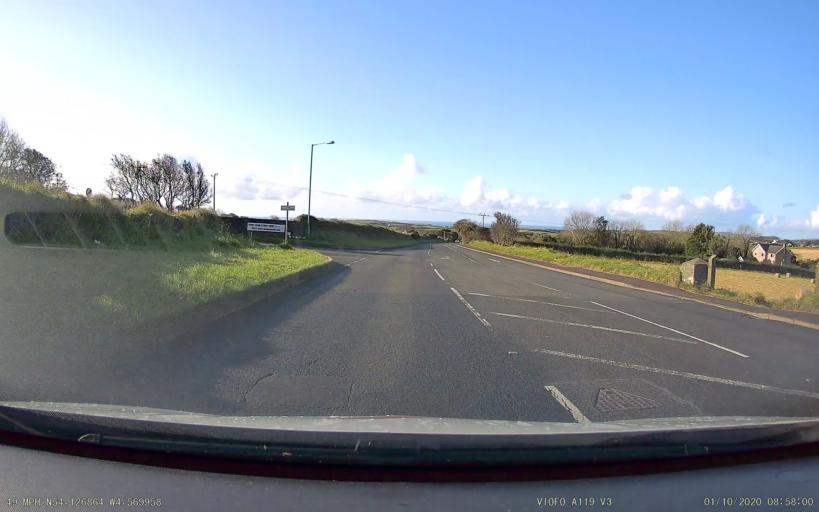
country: IM
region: Douglas
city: Douglas
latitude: 54.1269
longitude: -4.5700
